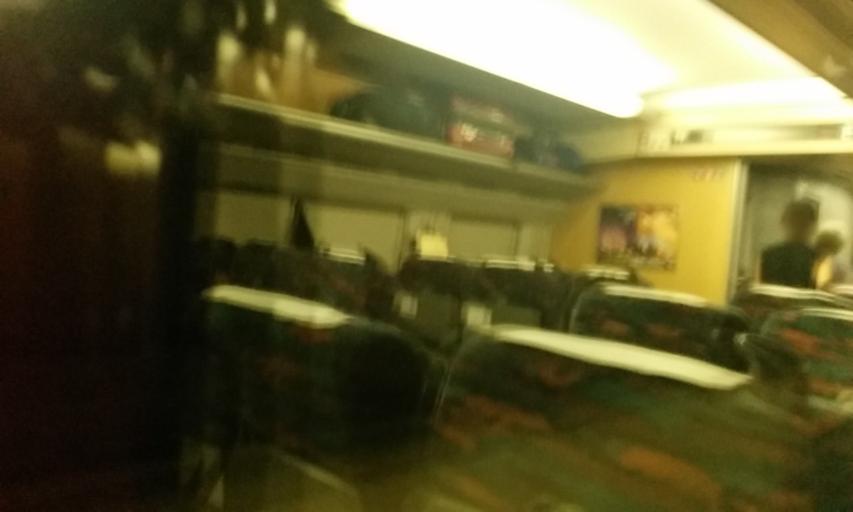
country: JP
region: Miyagi
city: Shiroishi
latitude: 38.0068
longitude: 140.6428
